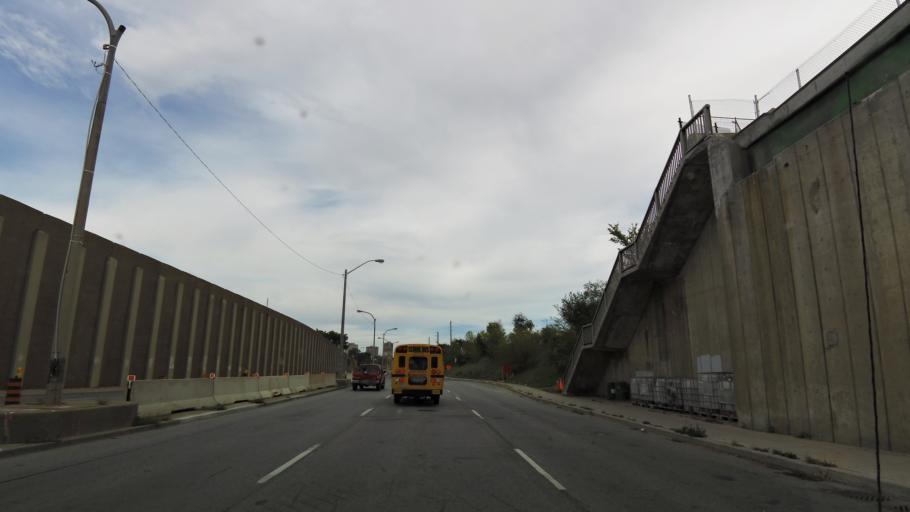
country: CA
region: Ontario
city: Toronto
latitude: 43.6875
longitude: -79.4865
